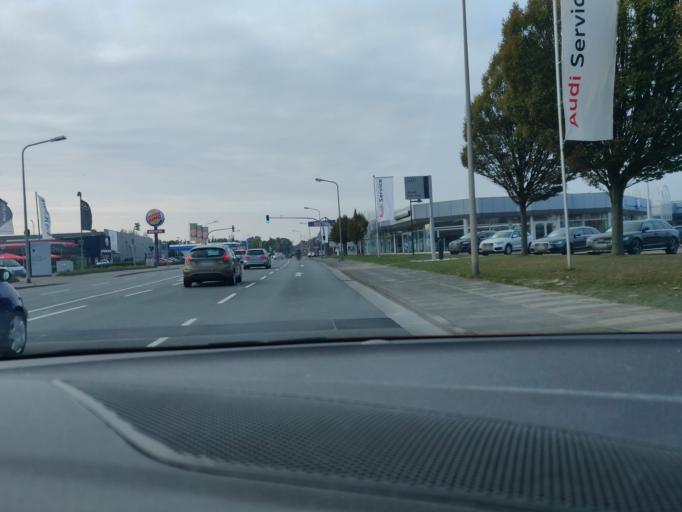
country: DE
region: Lower Saxony
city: Cuxhaven
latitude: 53.8520
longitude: 8.7142
